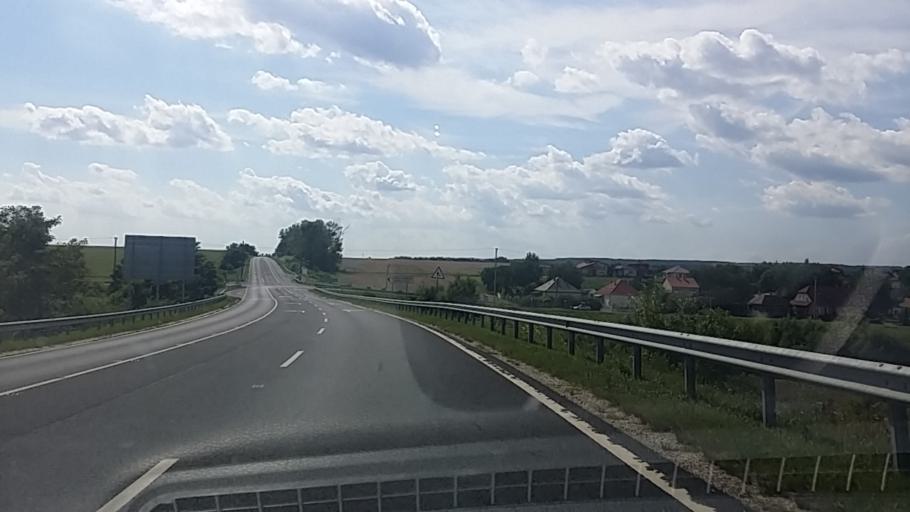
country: HU
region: Zala
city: Murakeresztur
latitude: 46.4588
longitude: 16.8837
